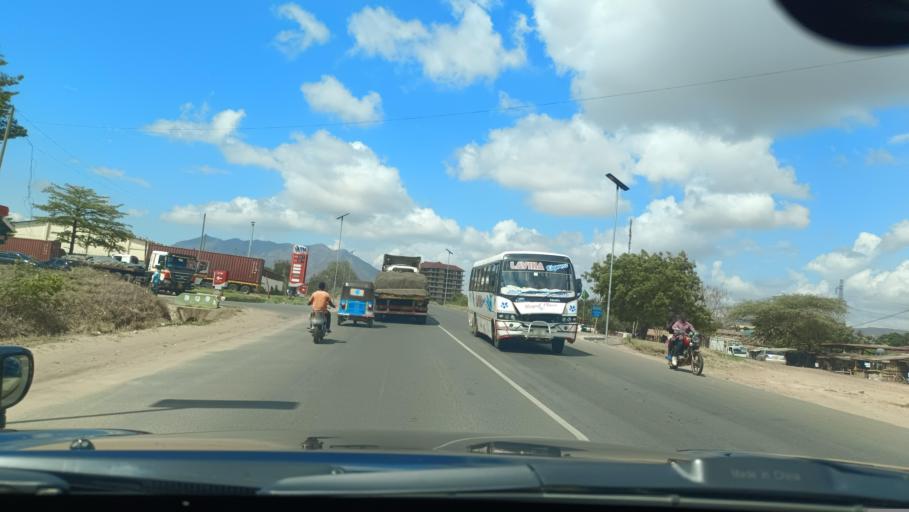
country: TZ
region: Morogoro
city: Morogoro
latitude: -6.8055
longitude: 37.6597
